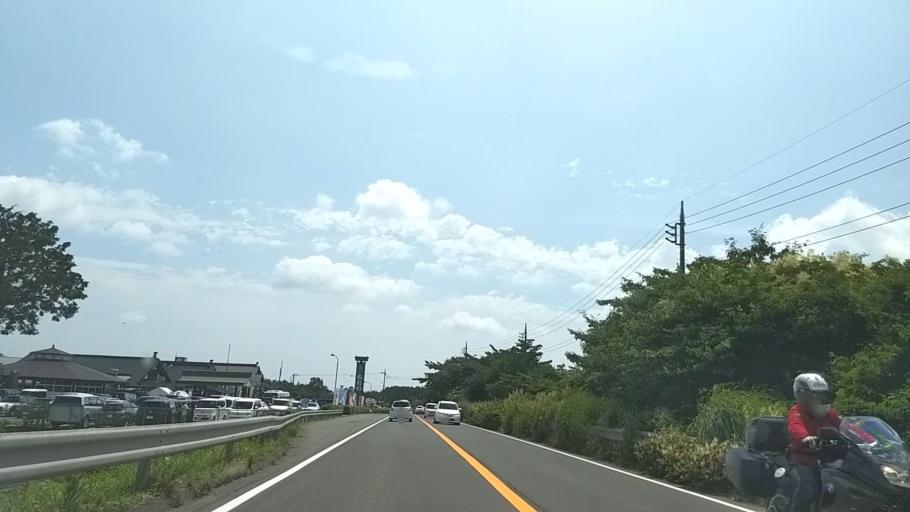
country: JP
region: Shizuoka
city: Fujinomiya
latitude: 35.3724
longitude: 138.5760
